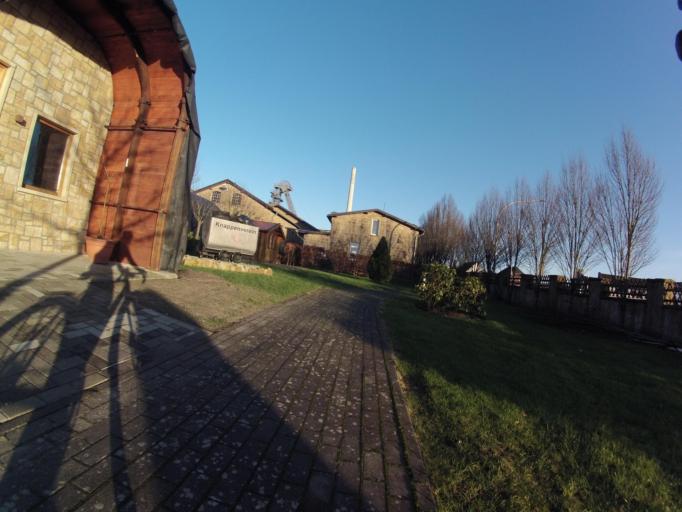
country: DE
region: North Rhine-Westphalia
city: Ibbenburen
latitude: 52.2873
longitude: 7.7345
